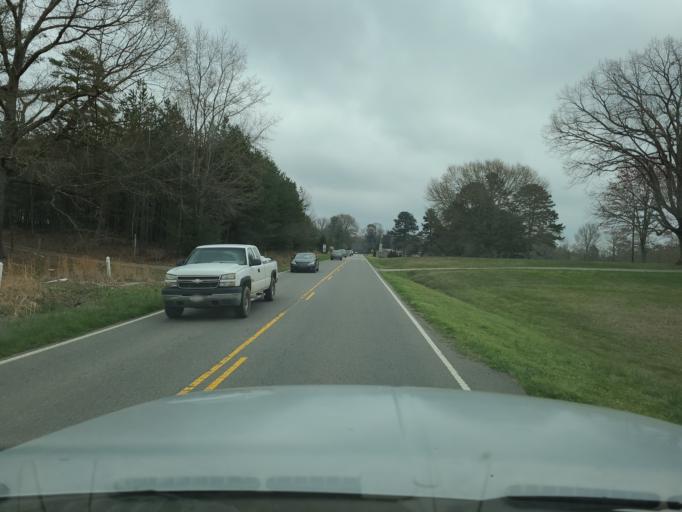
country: US
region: North Carolina
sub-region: Cleveland County
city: Shelby
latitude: 35.3854
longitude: -81.6216
